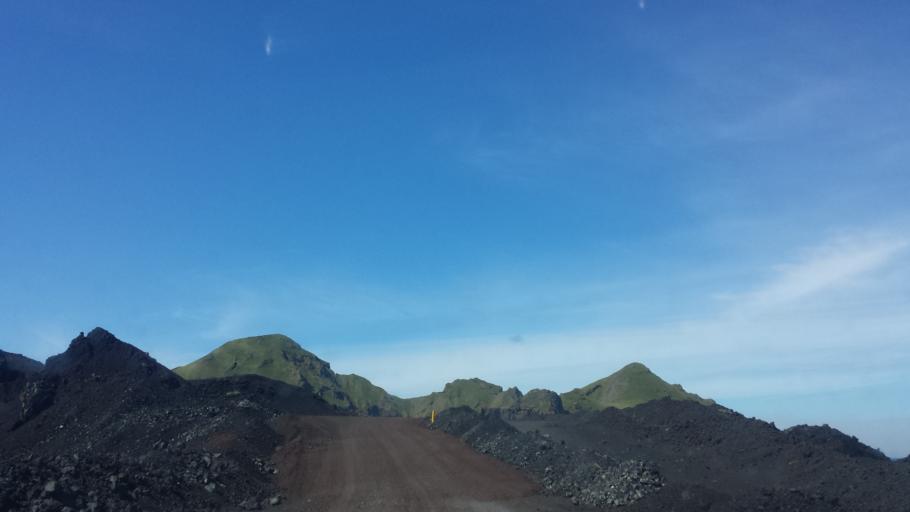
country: IS
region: South
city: Vestmannaeyjar
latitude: 63.4389
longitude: -20.2309
